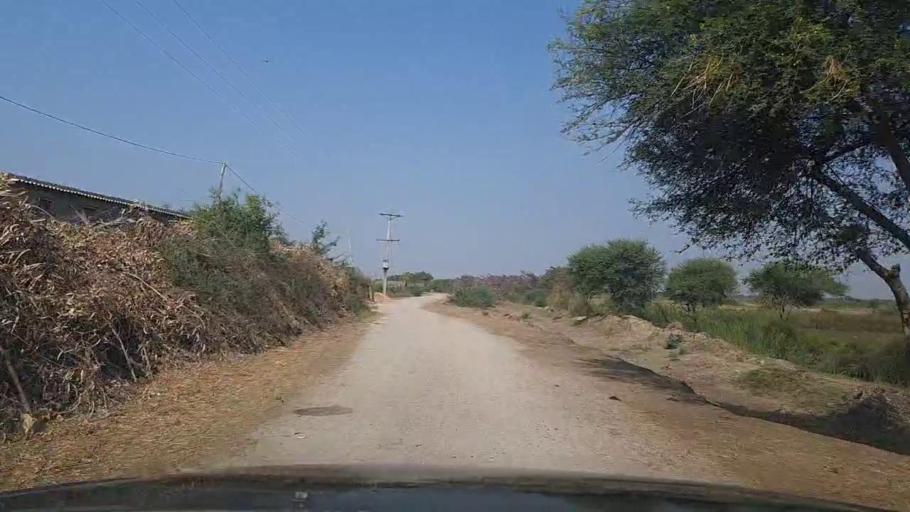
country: PK
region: Sindh
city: Thatta
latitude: 24.6161
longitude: 67.8189
